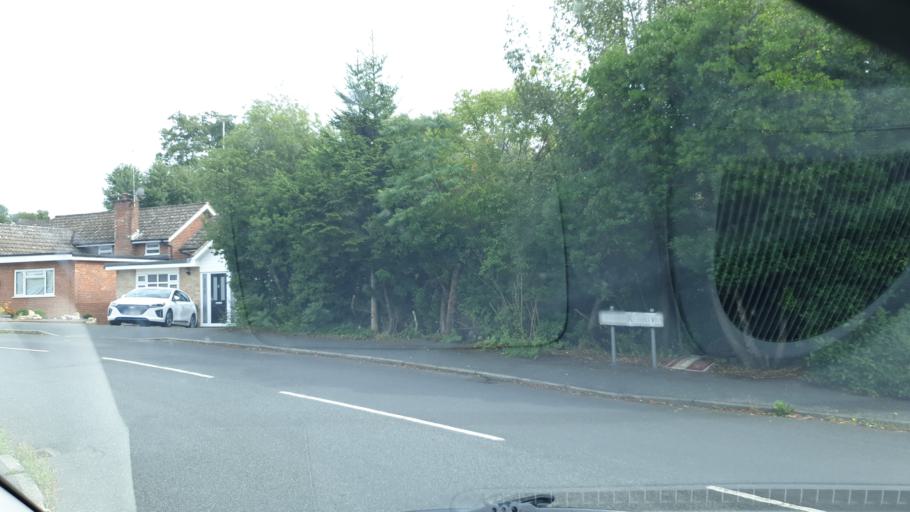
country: GB
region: England
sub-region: West Sussex
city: East Grinstead
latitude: 51.1361
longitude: 0.0056
